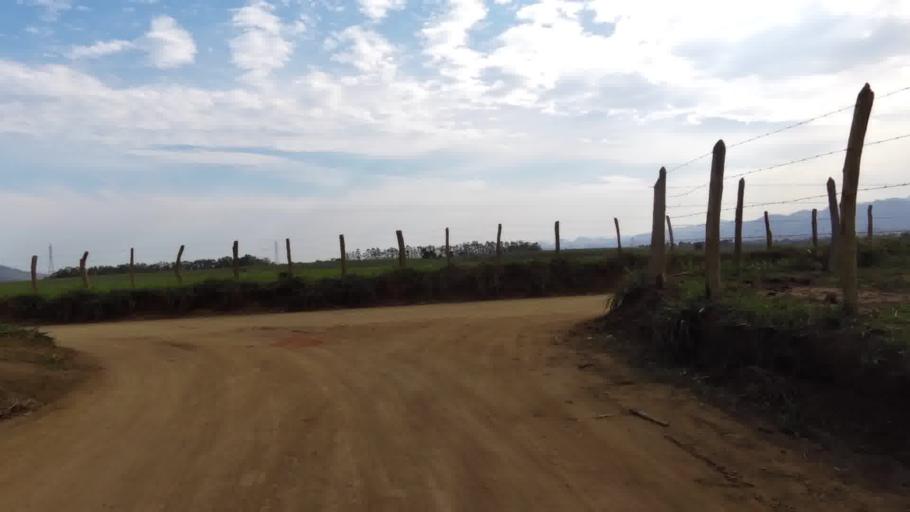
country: BR
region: Espirito Santo
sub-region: Piuma
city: Piuma
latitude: -20.8229
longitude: -40.7472
